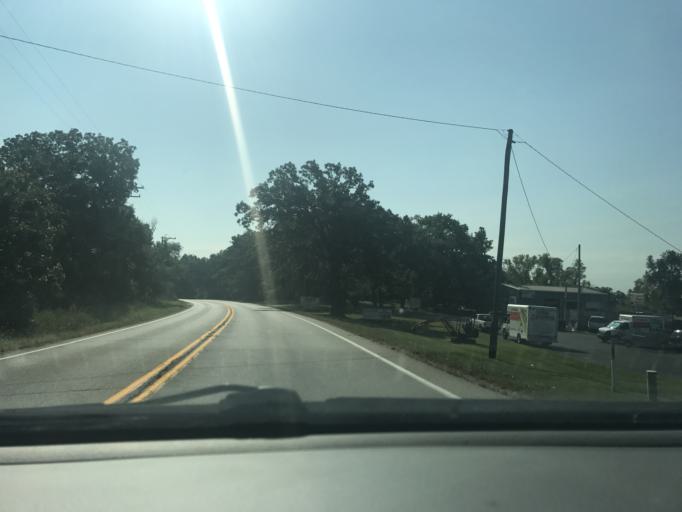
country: US
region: Illinois
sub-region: Kane County
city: Pingree Grove
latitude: 42.0671
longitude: -88.4338
